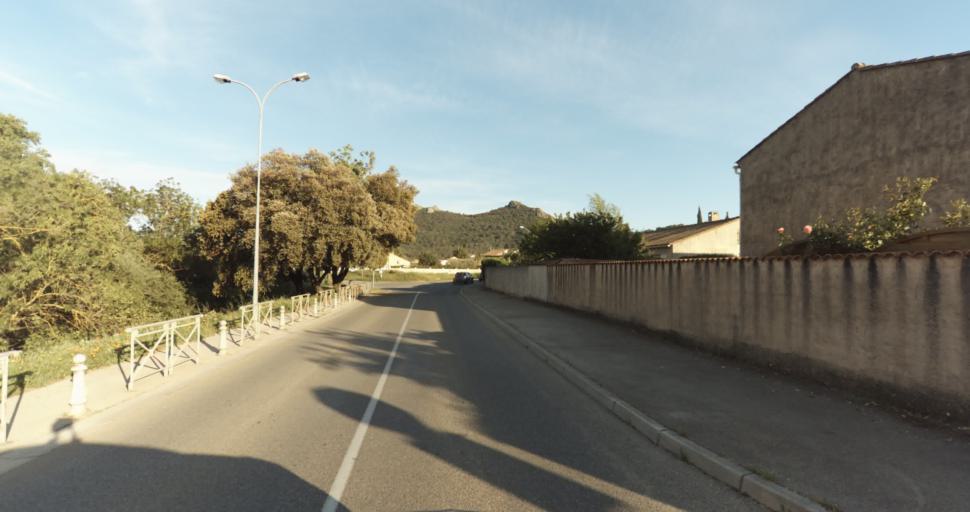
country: FR
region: Provence-Alpes-Cote d'Azur
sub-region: Departement du Var
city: La Crau
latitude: 43.1475
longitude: 6.0849
